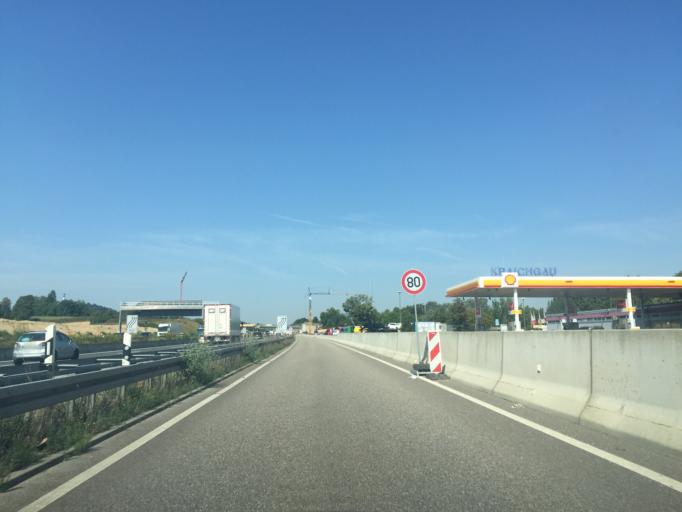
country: DE
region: Baden-Wuerttemberg
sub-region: Karlsruhe Region
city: Sinsheim
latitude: 49.2430
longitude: 8.8823
